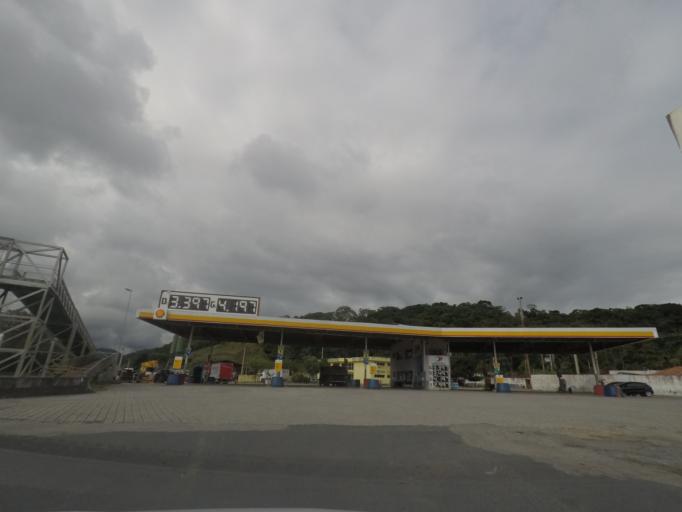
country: BR
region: Sao Paulo
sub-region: Miracatu
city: Miracatu
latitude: -24.1515
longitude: -47.3169
